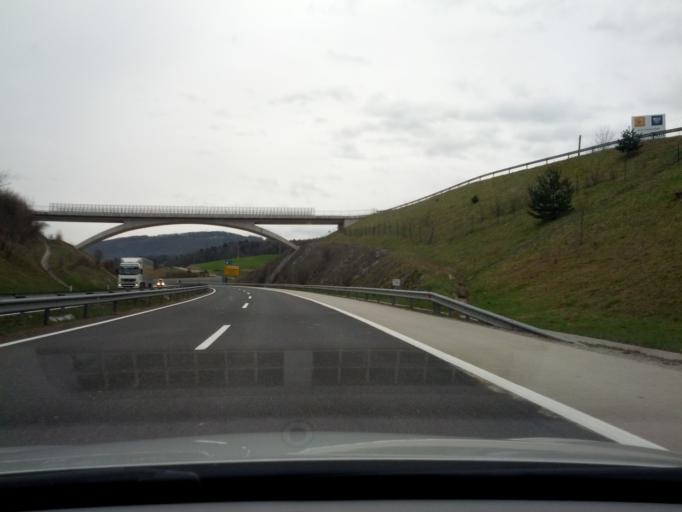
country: SI
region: Trebnje
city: Trebnje
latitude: 45.9118
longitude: 14.9594
